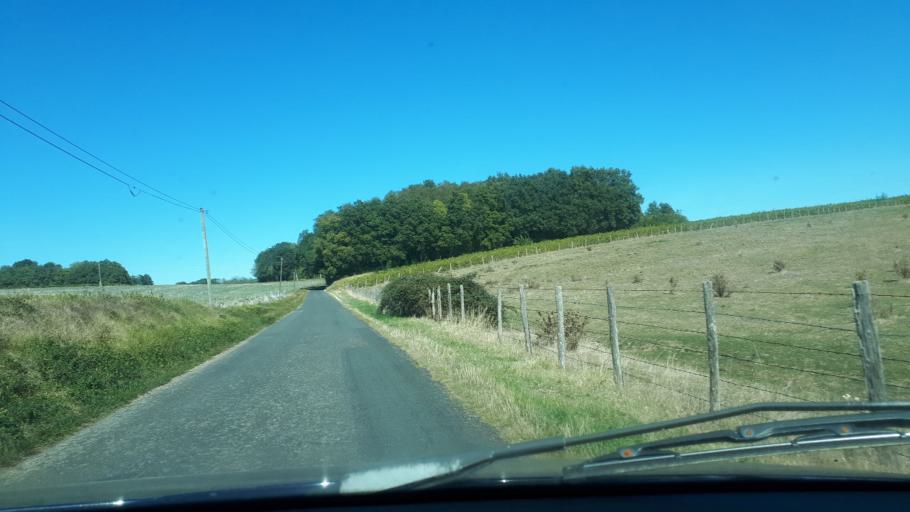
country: FR
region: Centre
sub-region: Departement du Loir-et-Cher
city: Villiers-sur-Loir
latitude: 47.8089
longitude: 1.0054
